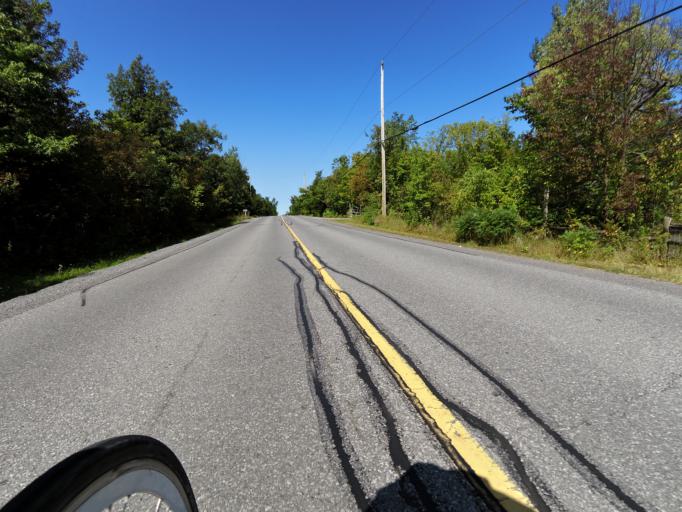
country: CA
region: Ontario
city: Bells Corners
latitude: 45.3986
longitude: -76.0168
